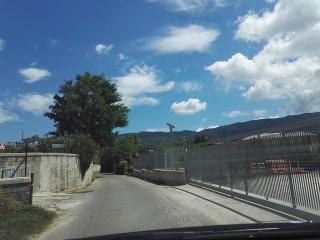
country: IT
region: Calabria
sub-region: Provincia di Vibo-Valentia
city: Serra San Bruno
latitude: 38.5756
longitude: 16.3199
